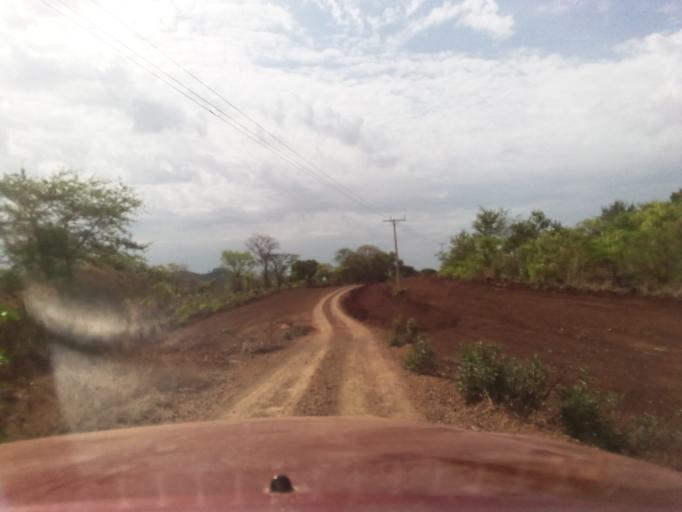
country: ET
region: Oromiya
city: Mendi
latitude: 10.0589
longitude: 35.2833
